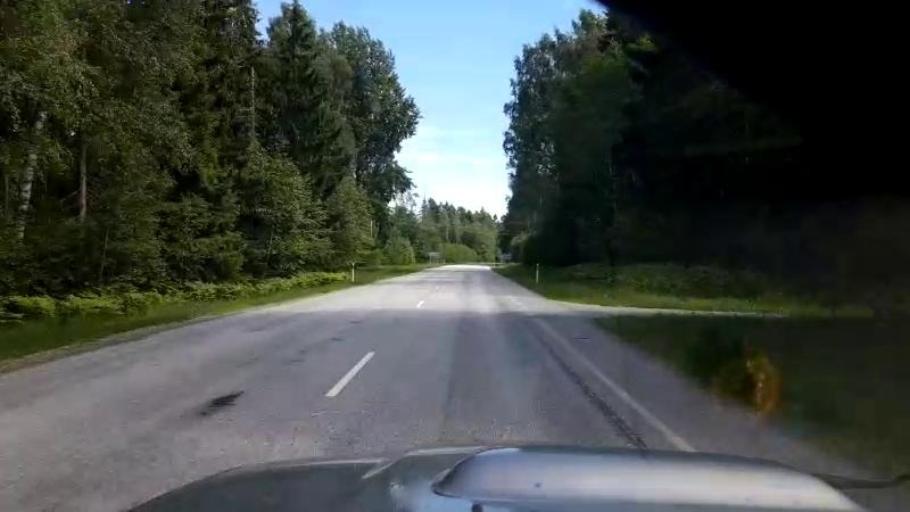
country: EE
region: Laeaene-Virumaa
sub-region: Rakke vald
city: Rakke
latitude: 58.9139
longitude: 26.2676
